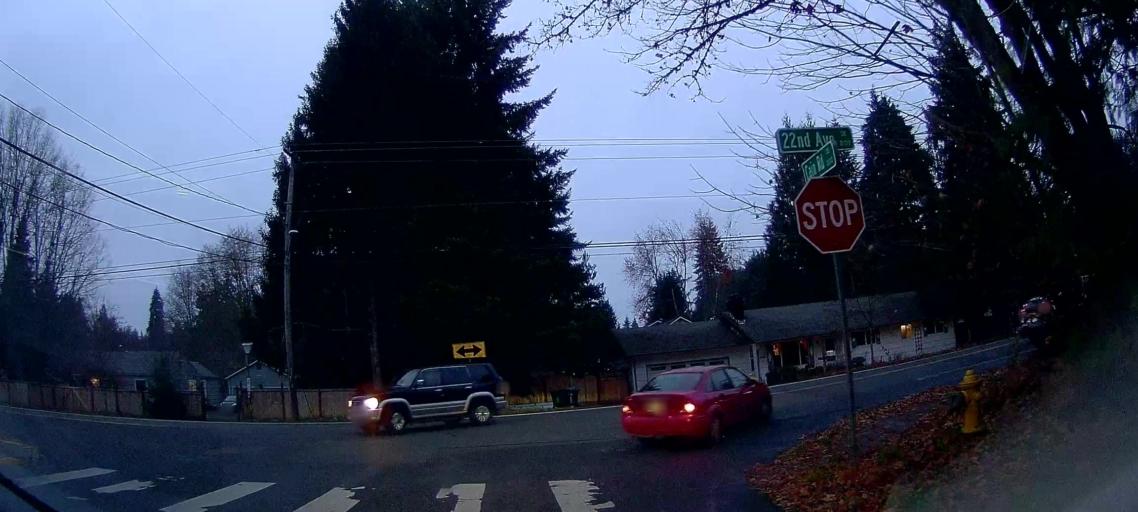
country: US
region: Washington
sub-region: Thurston County
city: Olympia
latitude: 47.0289
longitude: -122.8735
